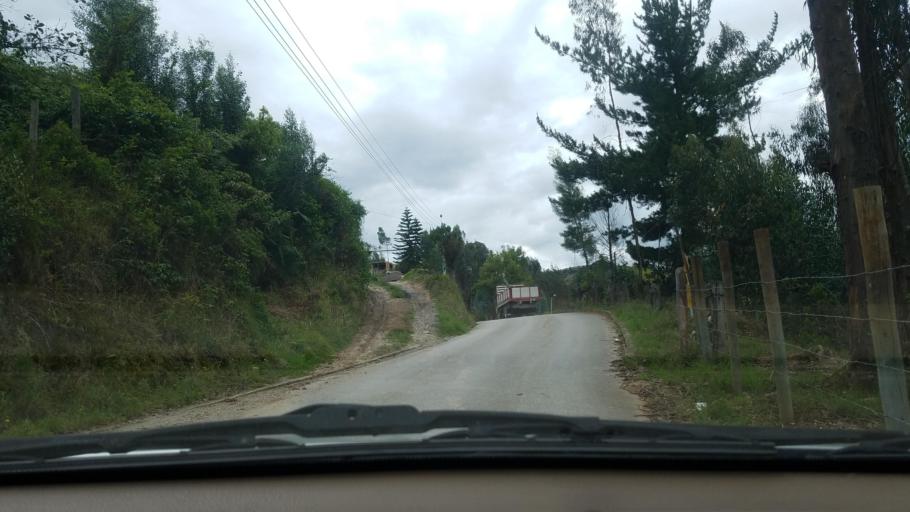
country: CO
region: Boyaca
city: Paipa
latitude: 5.7405
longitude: -73.1101
